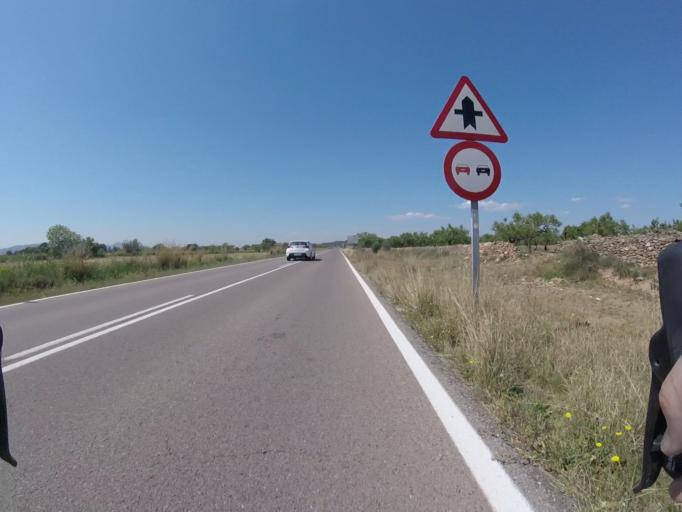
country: ES
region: Valencia
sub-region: Provincia de Castello
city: Benlloch
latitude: 40.2013
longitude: -0.0058
